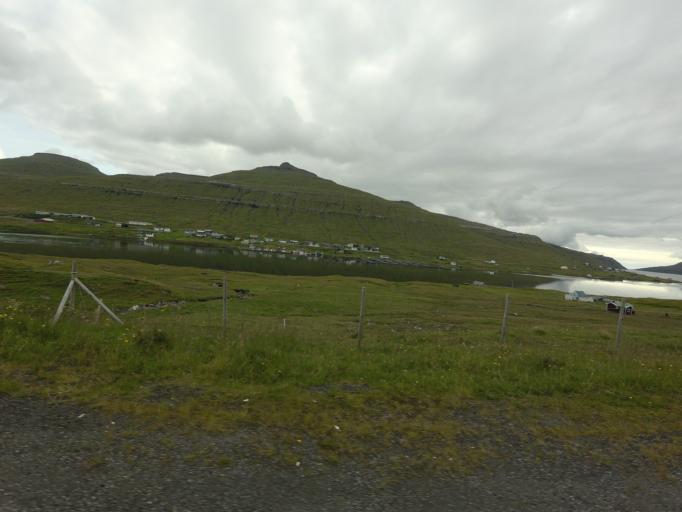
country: FO
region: Eysturoy
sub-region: Eidi
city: Eidi
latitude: 62.2014
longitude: -7.0094
